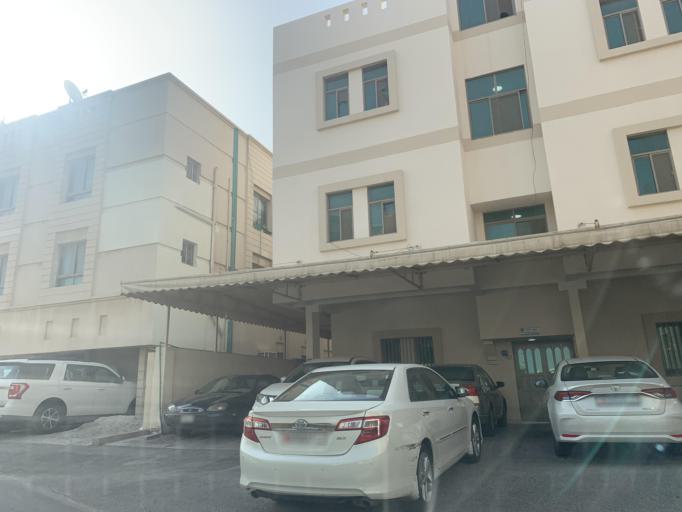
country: BH
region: Northern
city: Madinat `Isa
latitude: 26.1876
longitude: 50.5627
